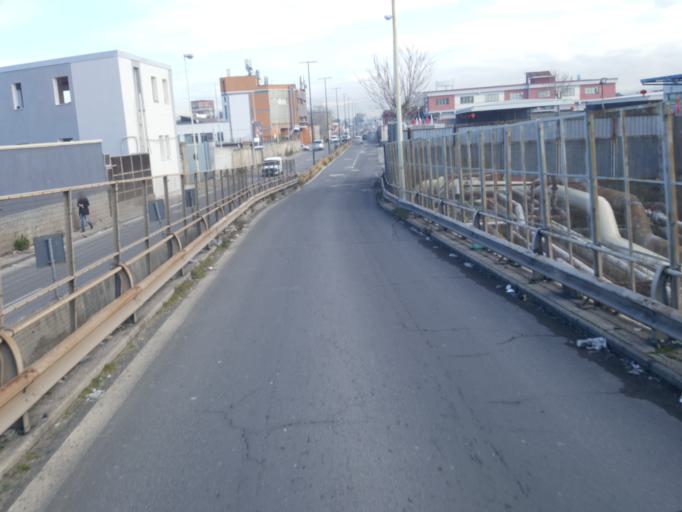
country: IT
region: Campania
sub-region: Provincia di Napoli
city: San Giorgio a Cremano
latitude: 40.8478
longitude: 14.3047
